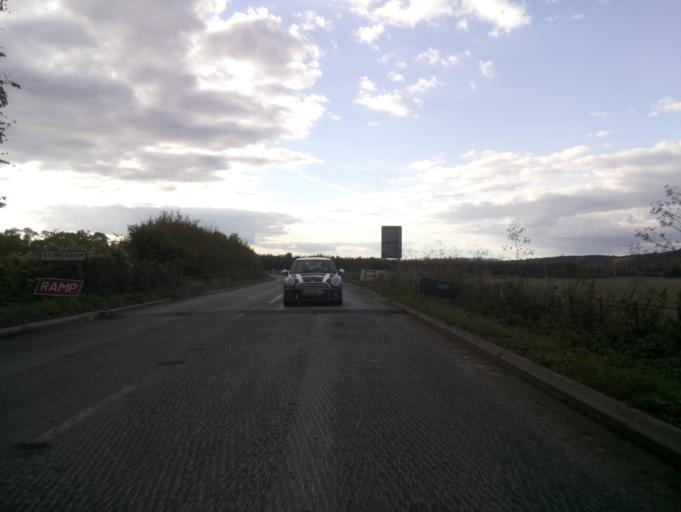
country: GB
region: England
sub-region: Herefordshire
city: Ocle Pychard
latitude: 52.0662
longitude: -2.5752
